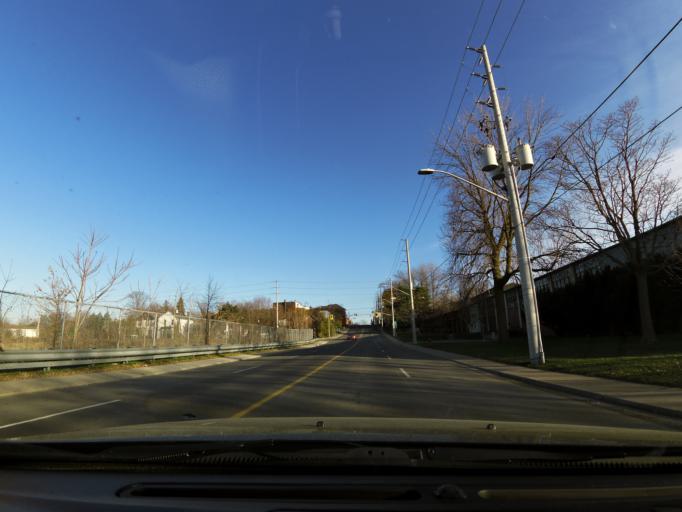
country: CA
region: Ontario
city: Hamilton
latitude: 43.2657
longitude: -79.8724
